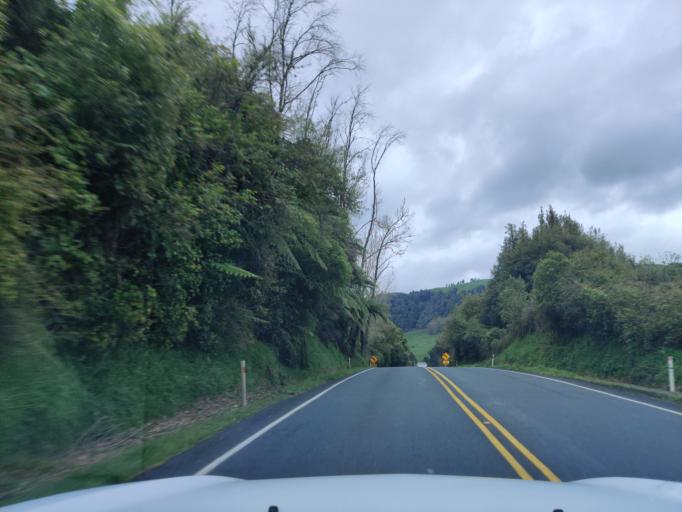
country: NZ
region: Waikato
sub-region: Otorohanga District
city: Otorohanga
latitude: -38.4943
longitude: 175.1889
